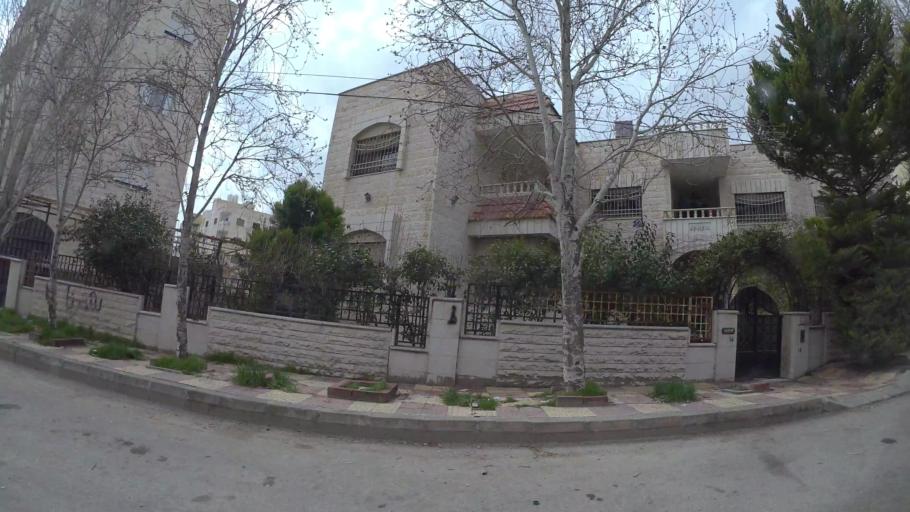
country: JO
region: Amman
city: Amman
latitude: 31.9905
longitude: 35.9269
